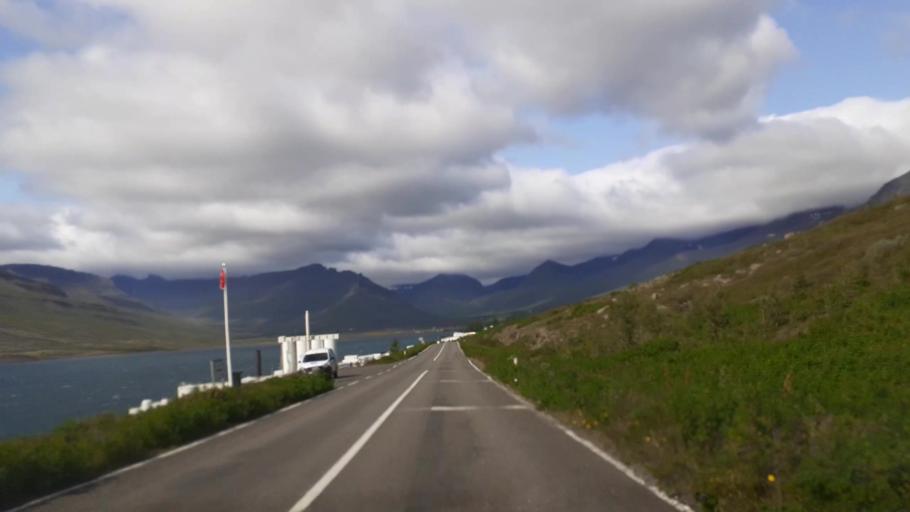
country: IS
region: East
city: Eskifjoerdur
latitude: 64.9238
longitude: -13.9815
